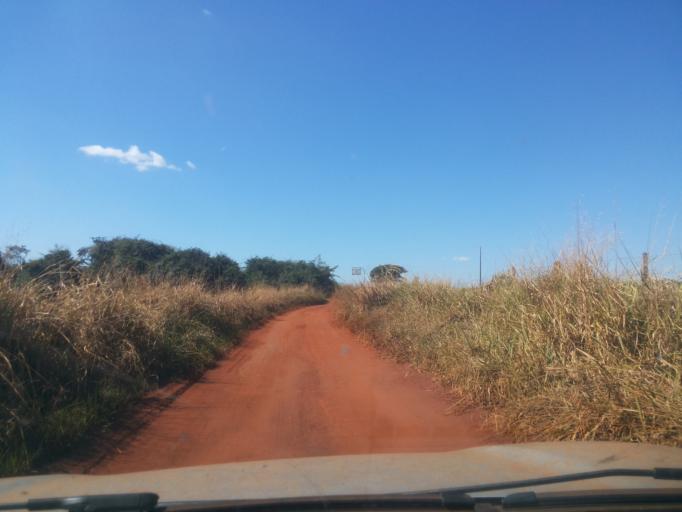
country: BR
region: Minas Gerais
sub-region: Centralina
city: Centralina
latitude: -18.7403
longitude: -49.1906
